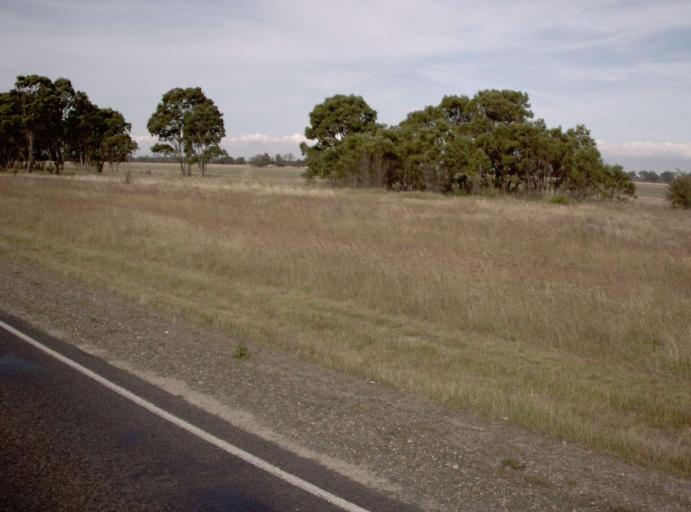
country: AU
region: Victoria
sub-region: Latrobe
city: Traralgon
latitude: -38.0800
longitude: 146.6086
